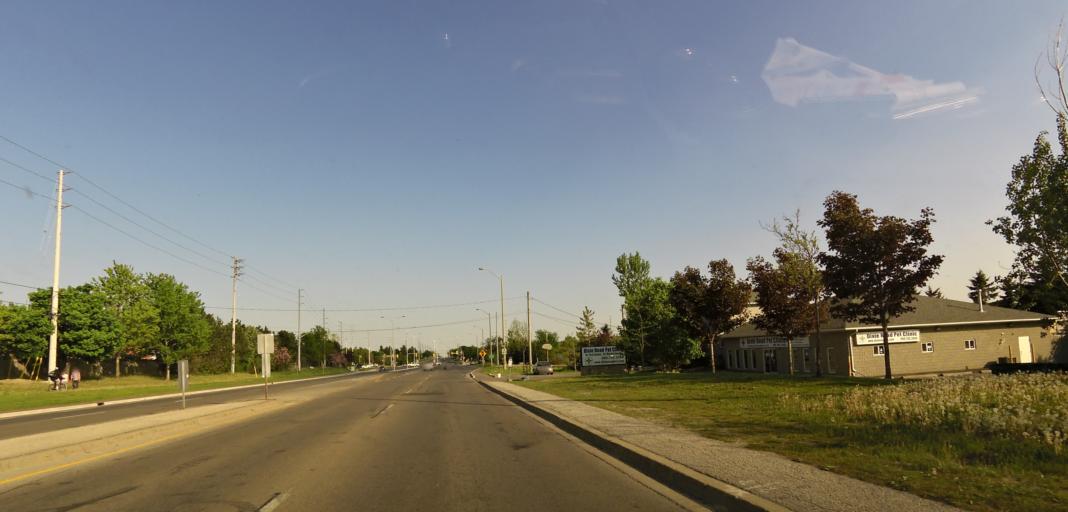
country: CA
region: Ontario
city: Brampton
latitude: 43.7365
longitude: -79.7572
